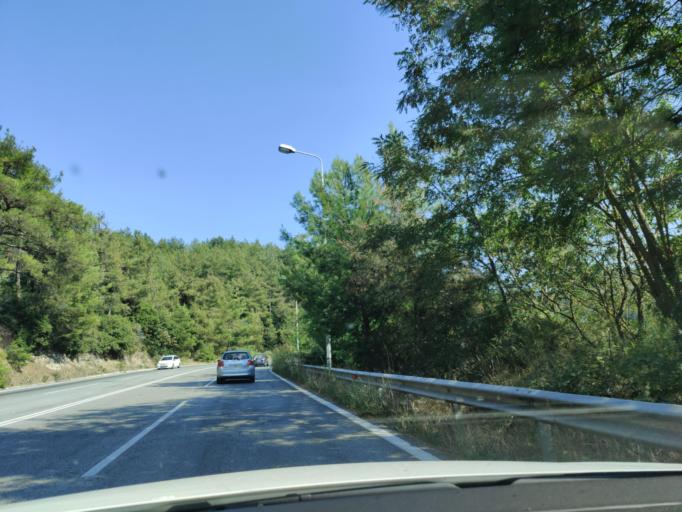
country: GR
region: East Macedonia and Thrace
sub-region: Nomos Kavalas
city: Amygdaleonas
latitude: 40.9486
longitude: 24.3708
